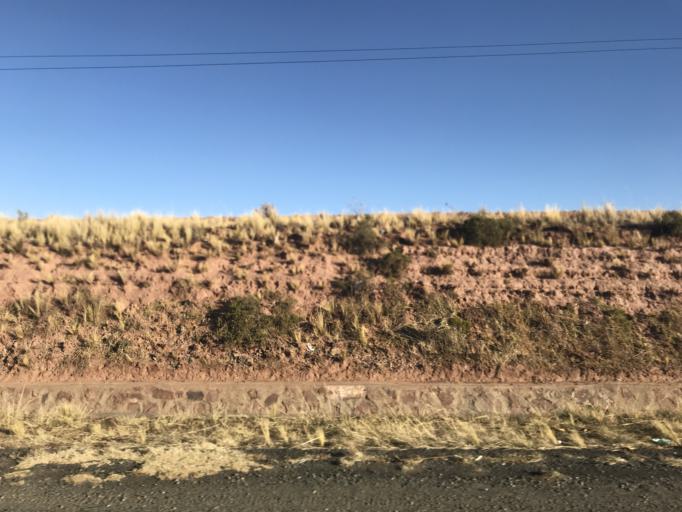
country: BO
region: La Paz
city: Tiahuanaco
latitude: -16.5652
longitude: -68.6391
